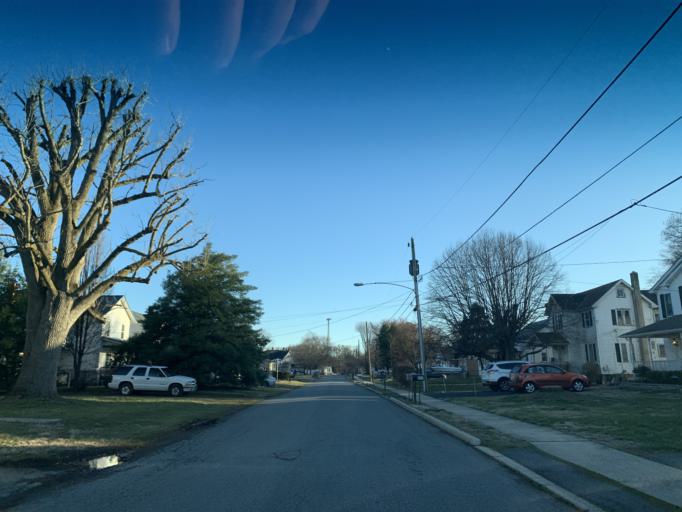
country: US
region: Maryland
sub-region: Cecil County
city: Perryville
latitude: 39.5633
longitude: -76.0697
